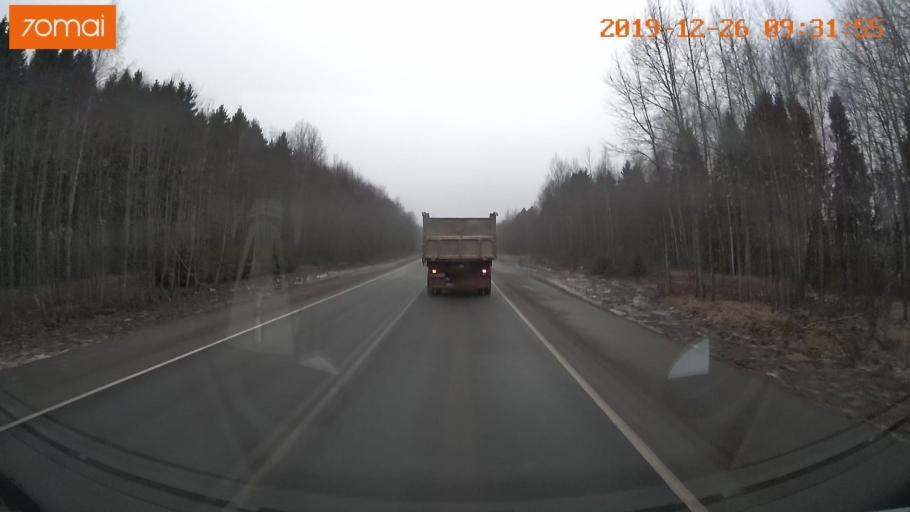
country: RU
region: Vologda
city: Gryazovets
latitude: 59.0733
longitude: 40.1225
